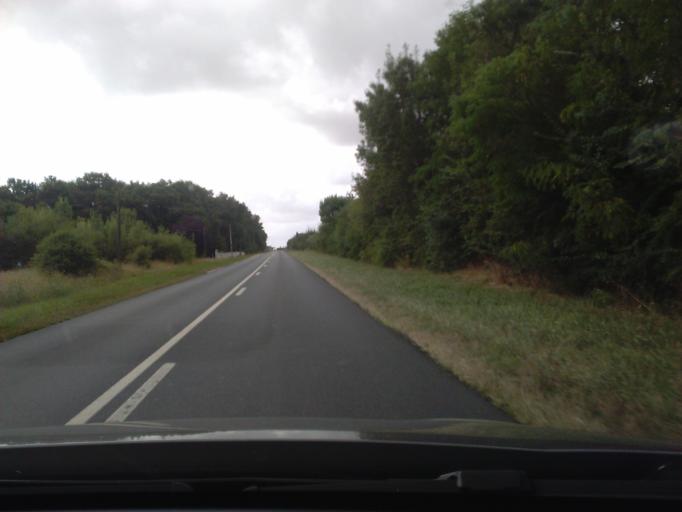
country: FR
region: Centre
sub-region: Departement du Loir-et-Cher
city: Cormeray
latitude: 47.5005
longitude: 1.4055
